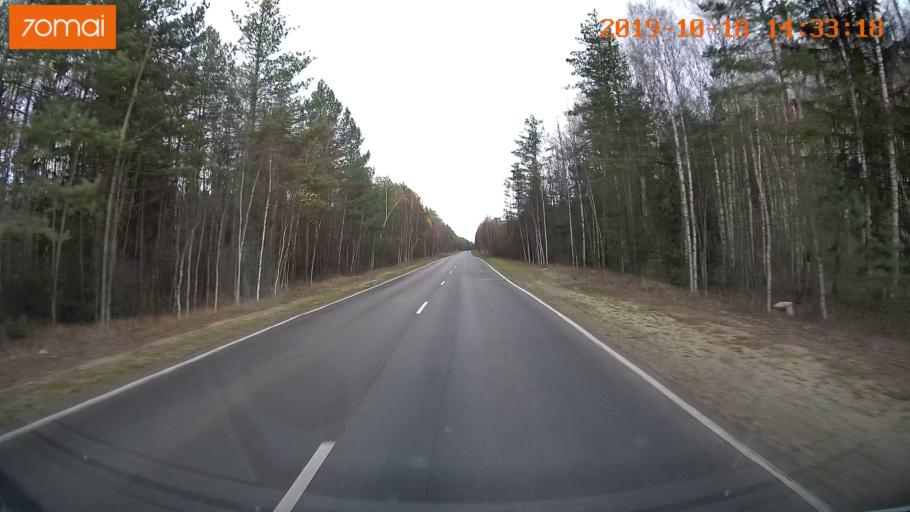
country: RU
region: Rjazan
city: Tuma
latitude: 55.1998
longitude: 40.5942
